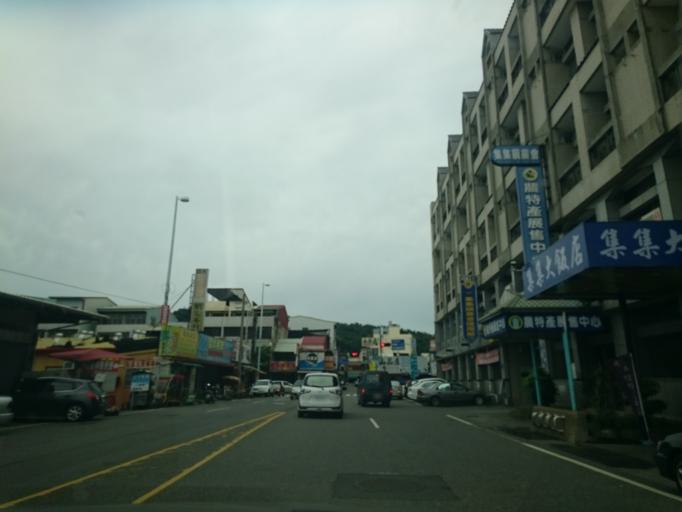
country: TW
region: Taiwan
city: Lugu
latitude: 23.8263
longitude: 120.7836
